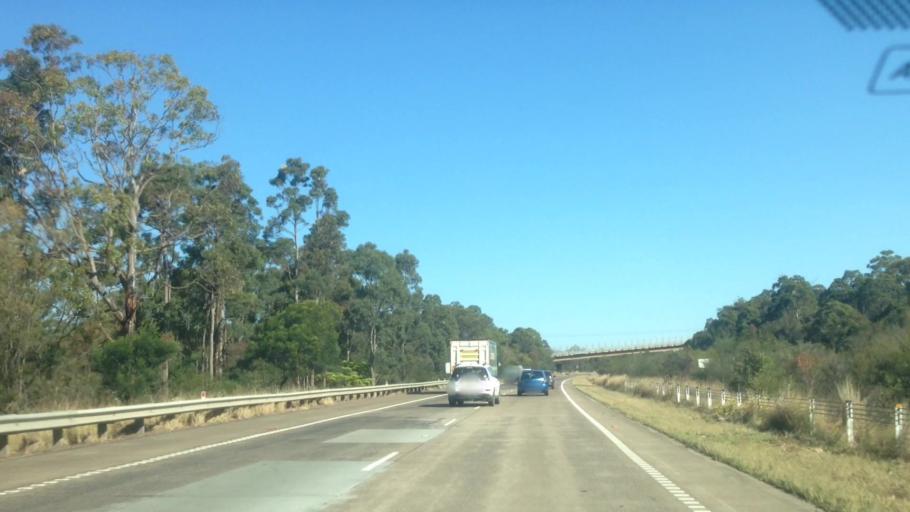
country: AU
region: New South Wales
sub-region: Wyong Shire
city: Charmhaven
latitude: -33.1902
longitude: 151.4674
